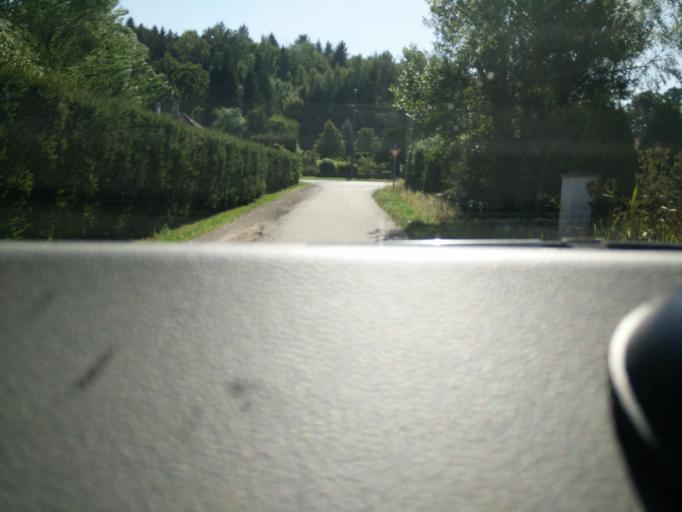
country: FR
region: Lorraine
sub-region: Departement des Vosges
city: Saulcy-sur-Meurthe
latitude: 48.2207
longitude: 6.9645
